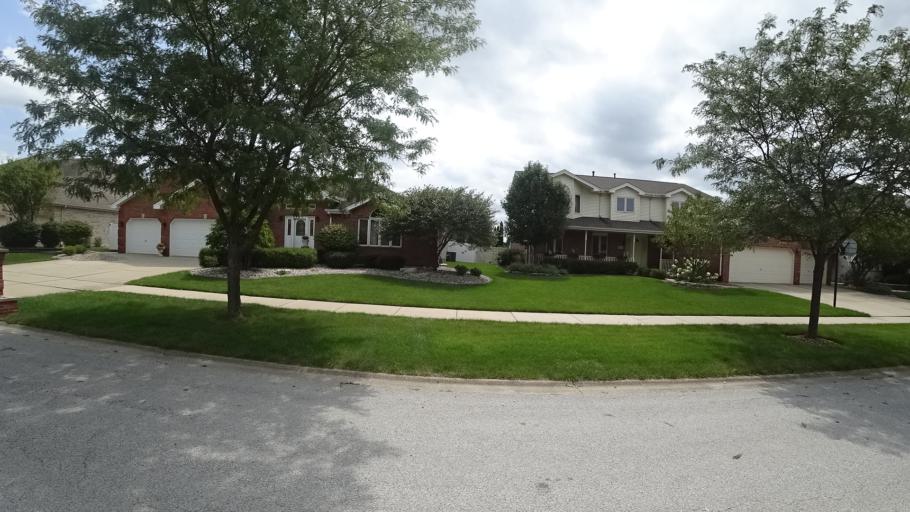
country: US
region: Illinois
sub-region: Cook County
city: Tinley Park
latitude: 41.5641
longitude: -87.8153
